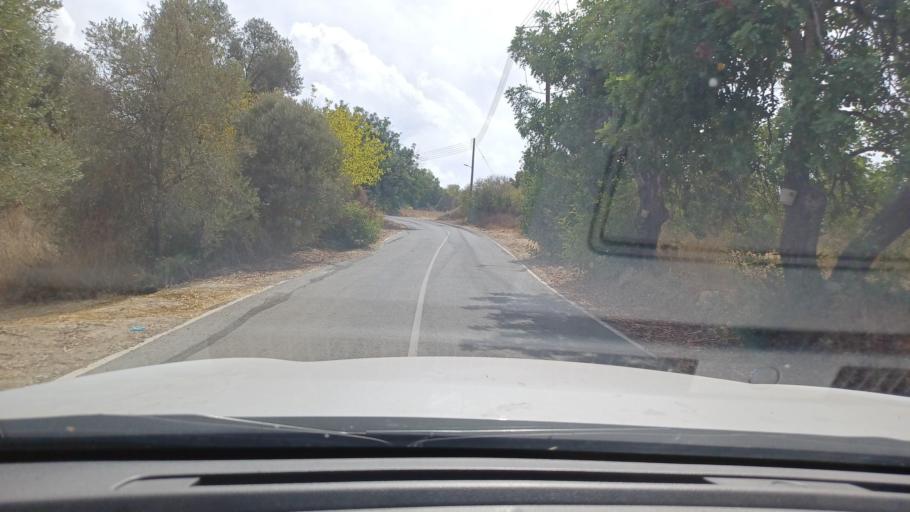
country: CY
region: Pafos
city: Pegeia
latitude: 34.9455
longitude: 32.4458
